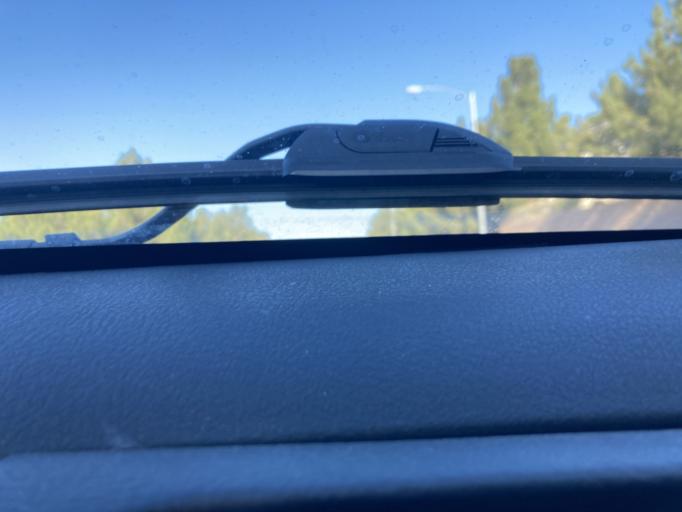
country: US
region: Nevada
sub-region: Clark County
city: Enterprise
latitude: 36.0592
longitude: -115.2901
